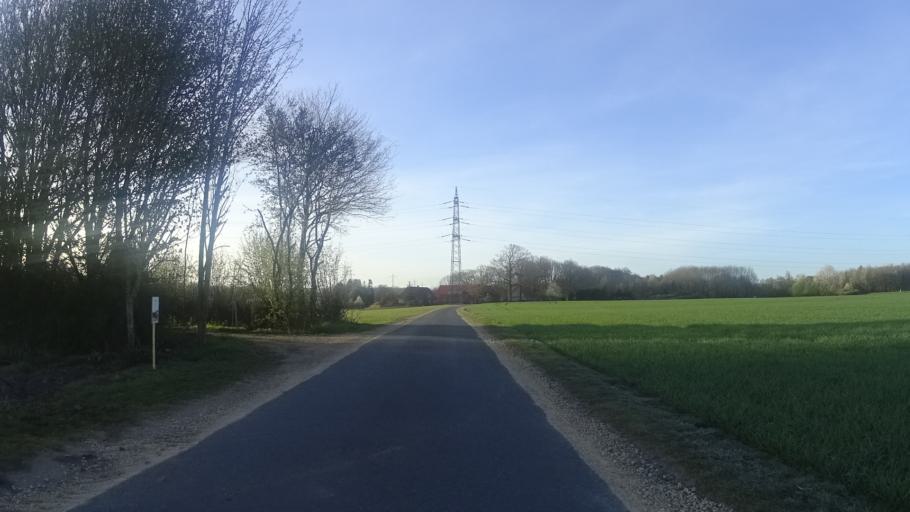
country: DE
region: North Rhine-Westphalia
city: Emsdetten
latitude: 52.2230
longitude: 7.5054
